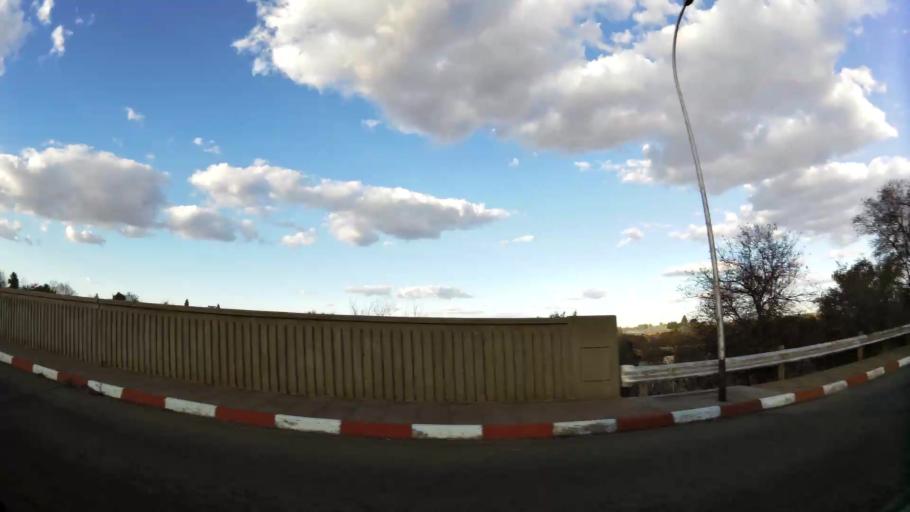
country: ZA
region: North-West
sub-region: Dr Kenneth Kaunda District Municipality
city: Potchefstroom
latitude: -26.6803
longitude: 27.0960
